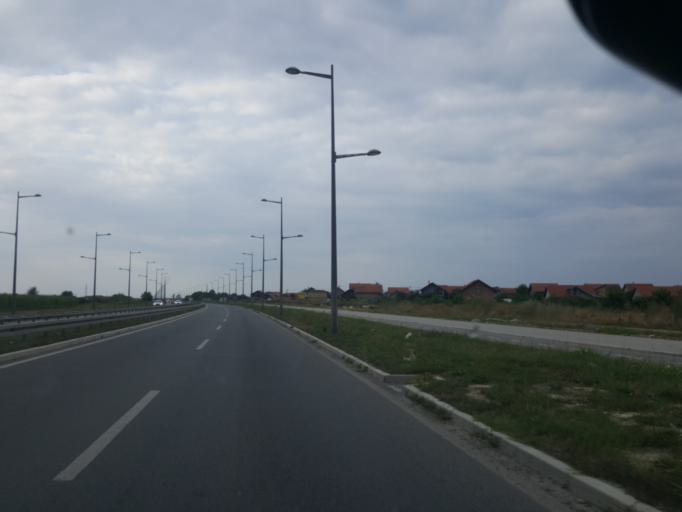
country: RS
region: Autonomna Pokrajina Vojvodina
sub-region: Juznobacki Okrug
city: Novi Sad
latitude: 45.2917
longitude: 19.8075
